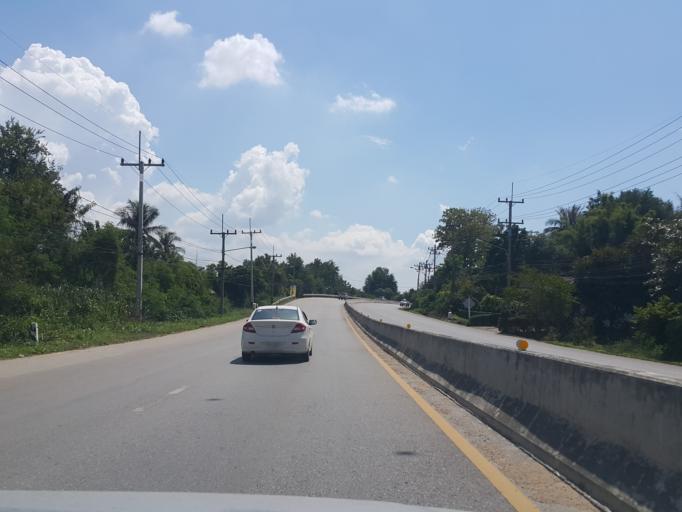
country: TH
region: Chiang Mai
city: Mae Taeng
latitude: 19.0612
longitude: 98.9412
